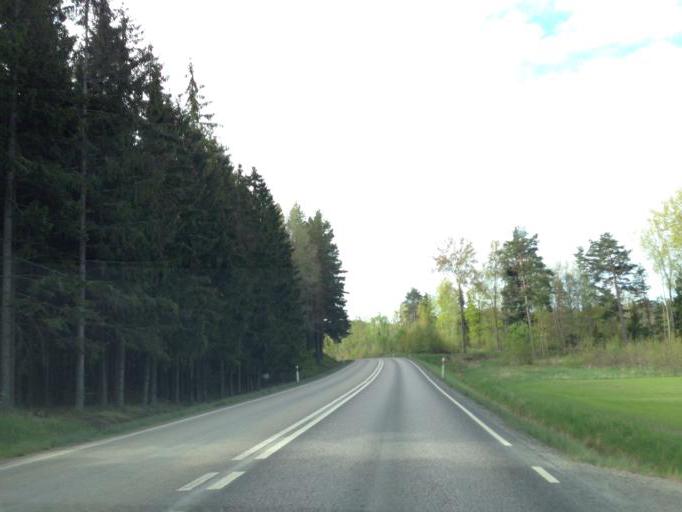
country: SE
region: Soedermanland
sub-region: Flens Kommun
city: Malmkoping
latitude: 59.0294
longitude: 16.8458
